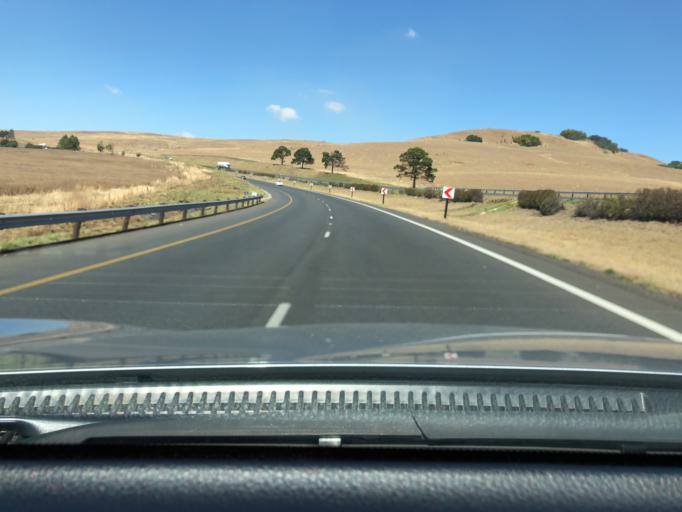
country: ZA
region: KwaZulu-Natal
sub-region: uThukela District Municipality
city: Estcourt
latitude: -29.1043
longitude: 29.9396
